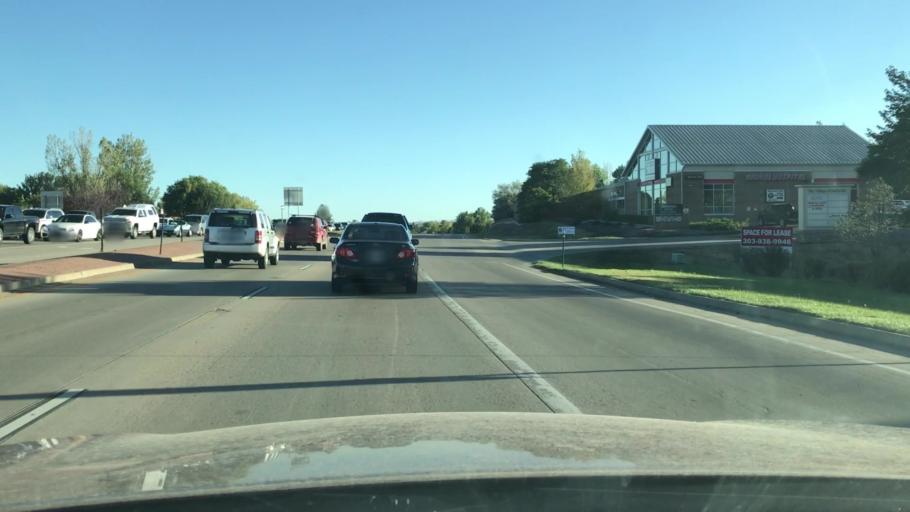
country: US
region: Colorado
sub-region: Boulder County
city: Lafayette
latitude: 39.9994
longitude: -105.1030
